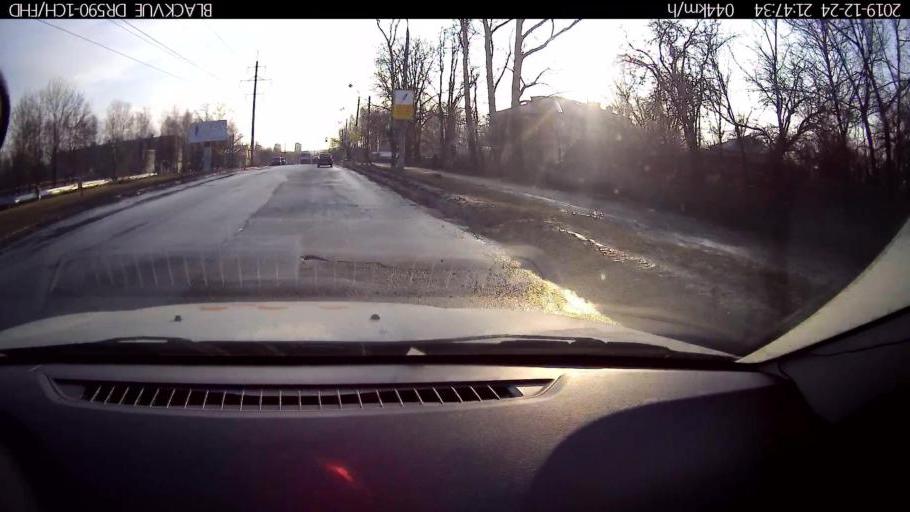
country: RU
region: Nizjnij Novgorod
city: Gorbatovka
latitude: 56.2294
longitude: 43.8413
